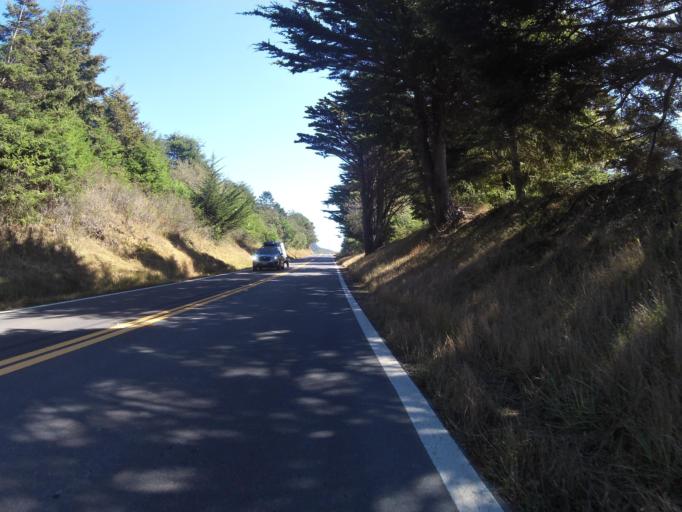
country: US
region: California
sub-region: Mendocino County
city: Fort Bragg
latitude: 39.5910
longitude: -123.7788
